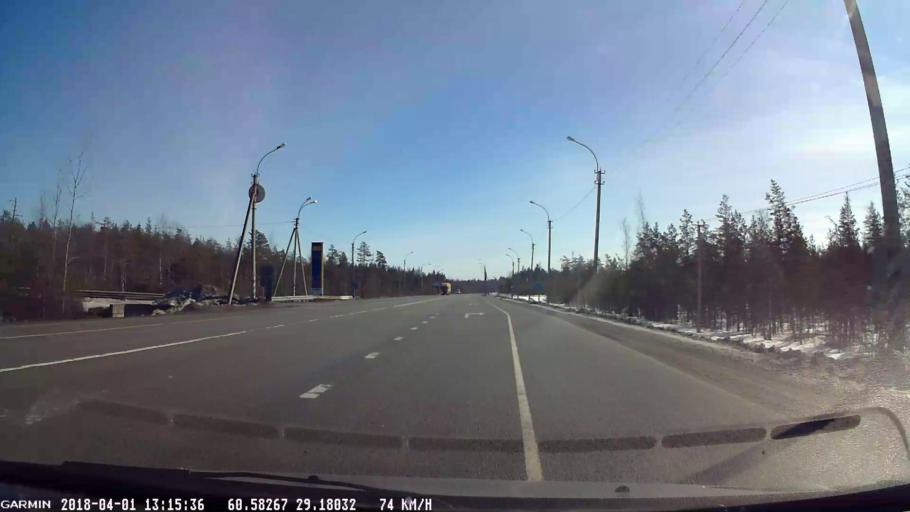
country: RU
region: Leningrad
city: Veshchevo
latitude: 60.5840
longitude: 29.1770
